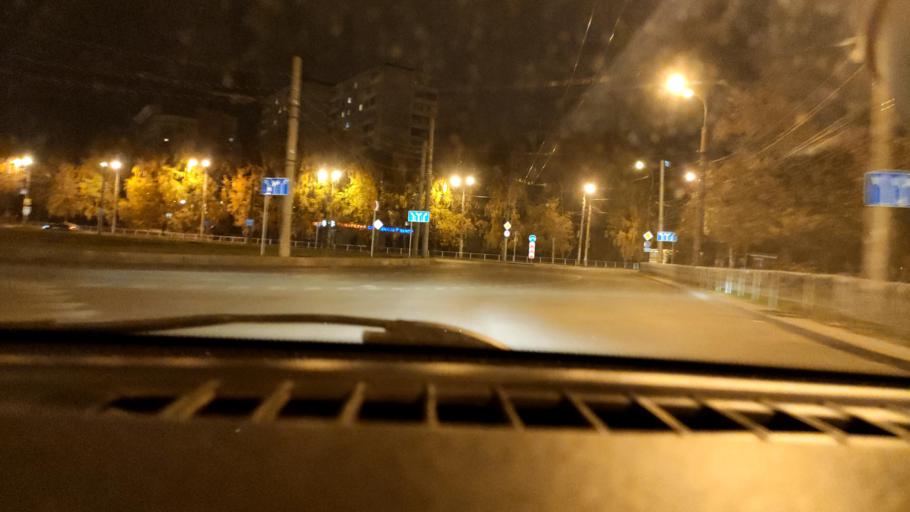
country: RU
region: Samara
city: Samara
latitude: 53.2435
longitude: 50.2321
